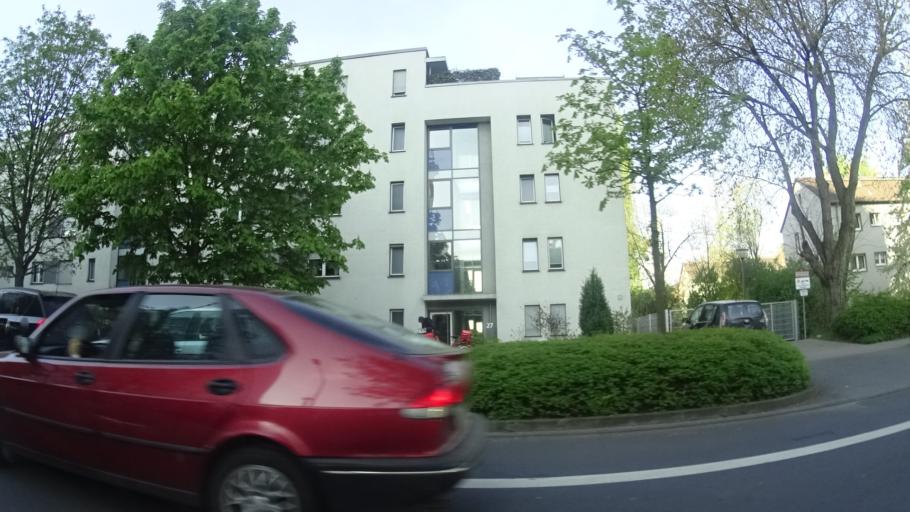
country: DE
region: Hesse
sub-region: Regierungsbezirk Darmstadt
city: Frankfurt am Main
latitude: 50.1348
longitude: 8.6756
